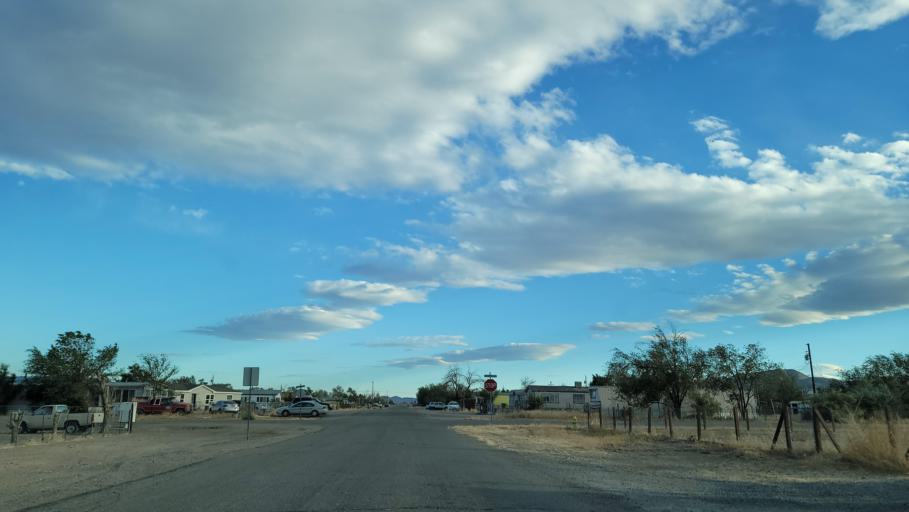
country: US
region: Nevada
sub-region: Lyon County
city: Silver Springs
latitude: 39.4094
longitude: -119.2220
